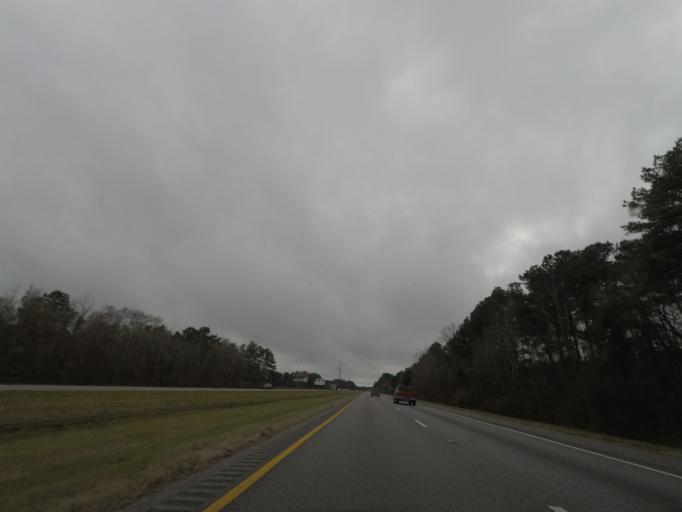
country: US
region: South Carolina
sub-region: Orangeburg County
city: Holly Hill
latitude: 33.4321
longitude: -80.4877
